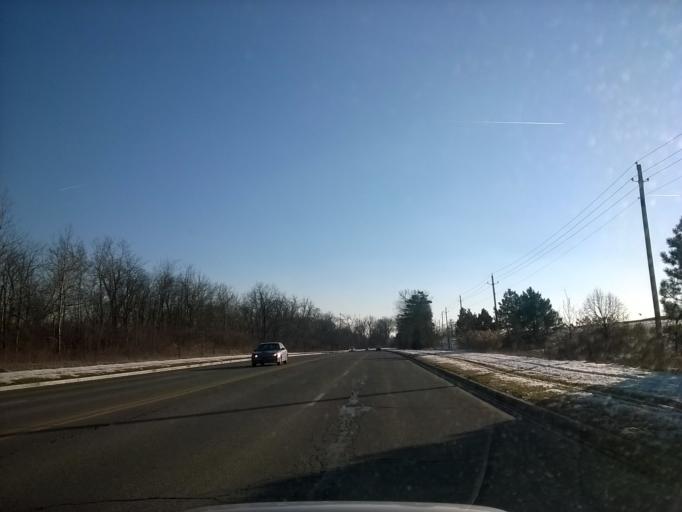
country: US
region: Indiana
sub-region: Hamilton County
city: Carmel
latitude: 39.9357
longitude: -86.0758
